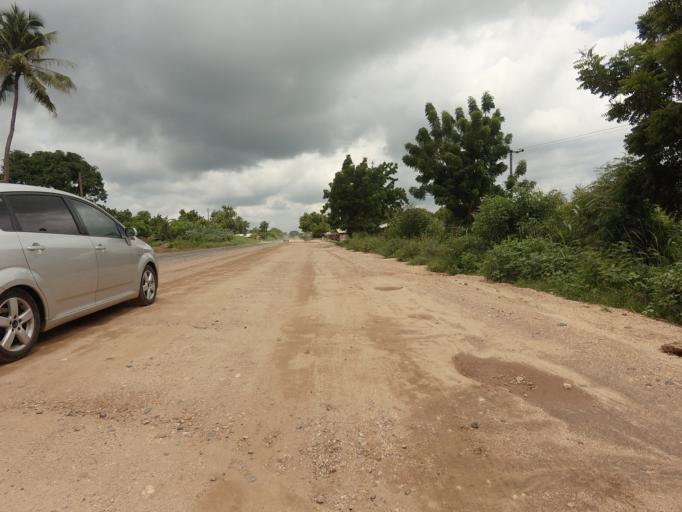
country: GH
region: Volta
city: Ho
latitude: 6.6500
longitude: 0.3003
